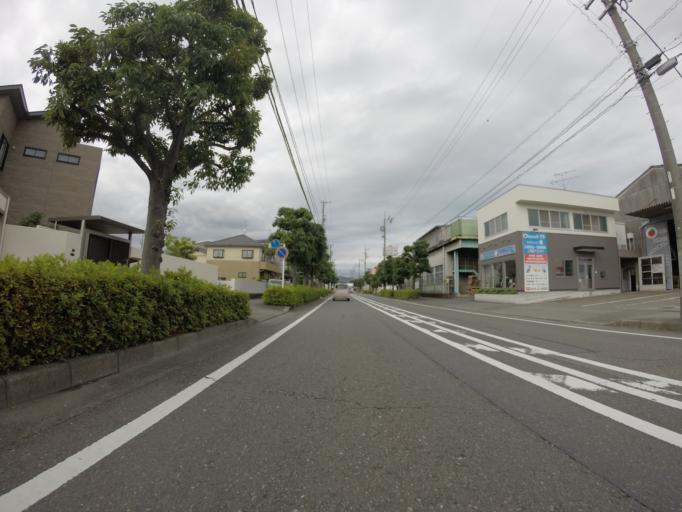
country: JP
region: Shizuoka
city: Shizuoka-shi
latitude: 35.0217
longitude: 138.4695
